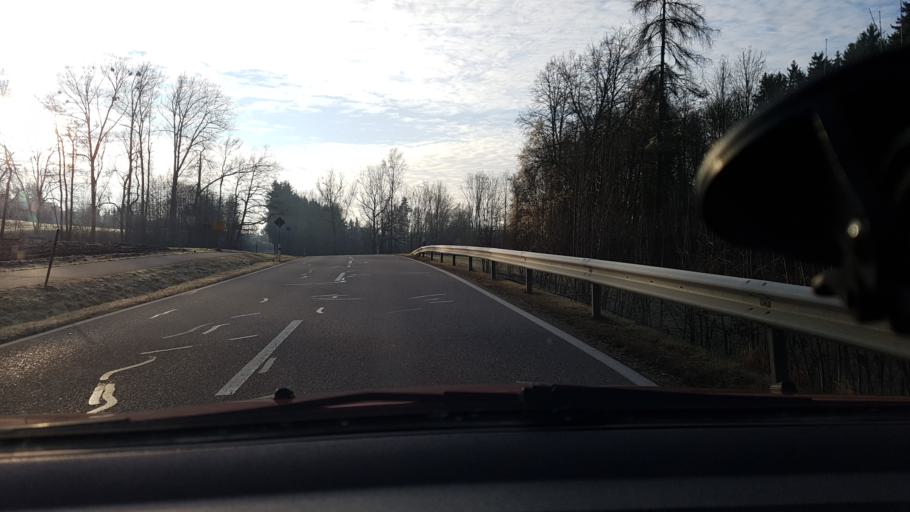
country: DE
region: Bavaria
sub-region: Lower Bavaria
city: Stubenberg
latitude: 48.2962
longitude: 13.0729
